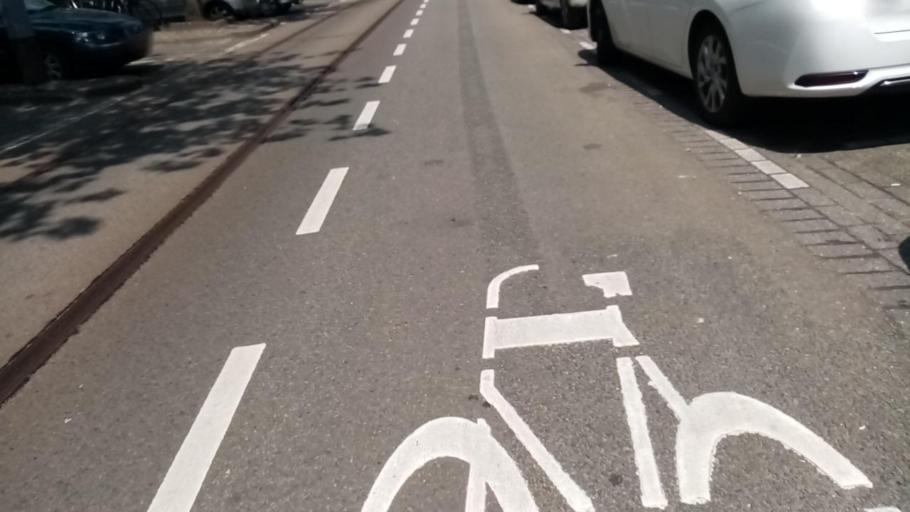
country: NL
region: South Holland
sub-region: Gemeente Rotterdam
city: Delfshaven
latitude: 51.9162
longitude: 4.4594
